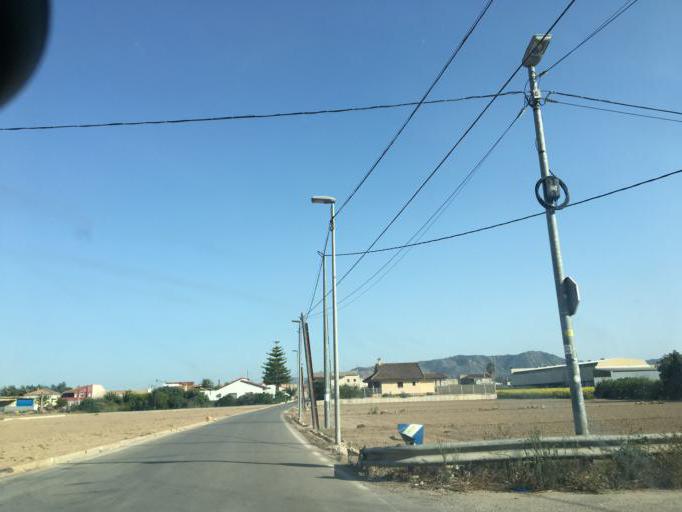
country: ES
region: Murcia
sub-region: Murcia
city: Santomera
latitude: 38.0306
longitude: -1.0679
